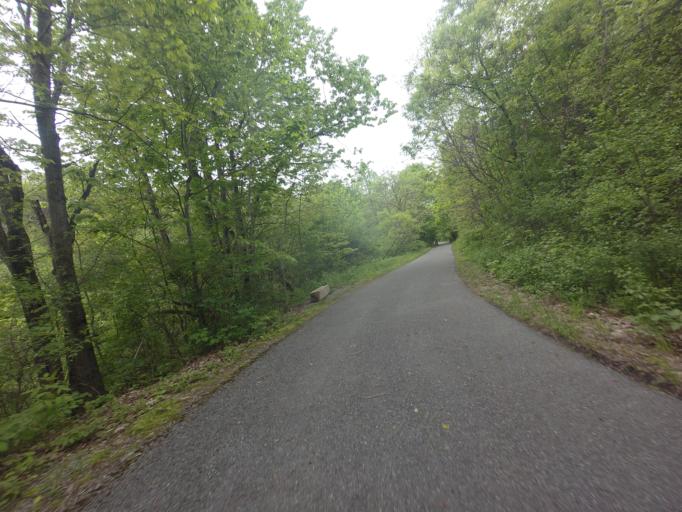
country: US
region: New York
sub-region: Jefferson County
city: Black River
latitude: 43.9925
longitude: -75.8220
